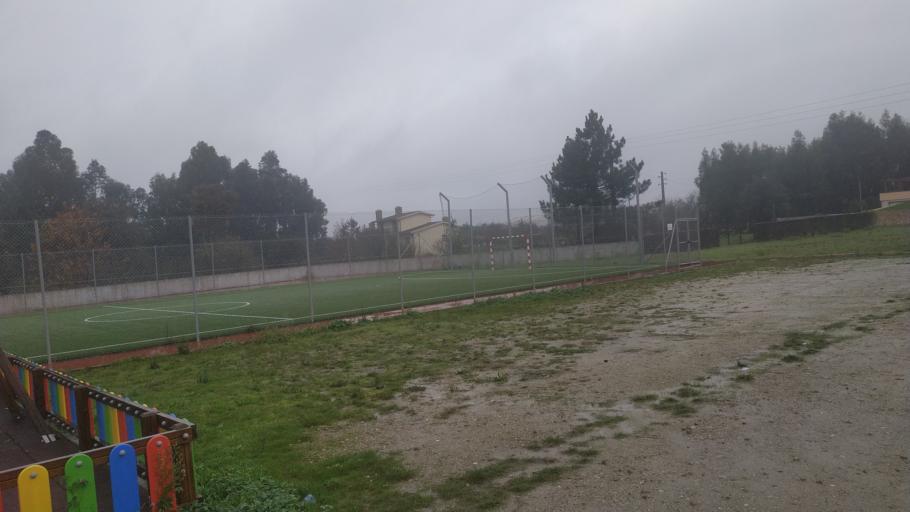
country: PT
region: Aveiro
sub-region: Albergaria-A-Velha
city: Branca
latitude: 40.7495
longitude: -8.4861
